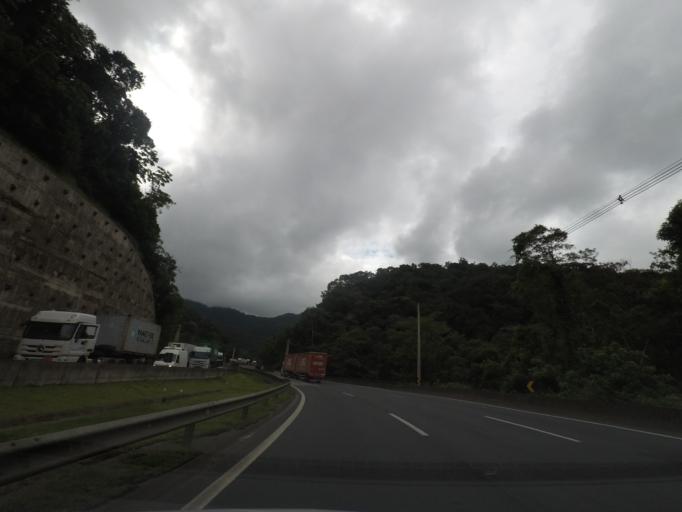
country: BR
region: Sao Paulo
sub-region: Juquitiba
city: Juquitiba
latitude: -24.0814
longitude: -47.2515
